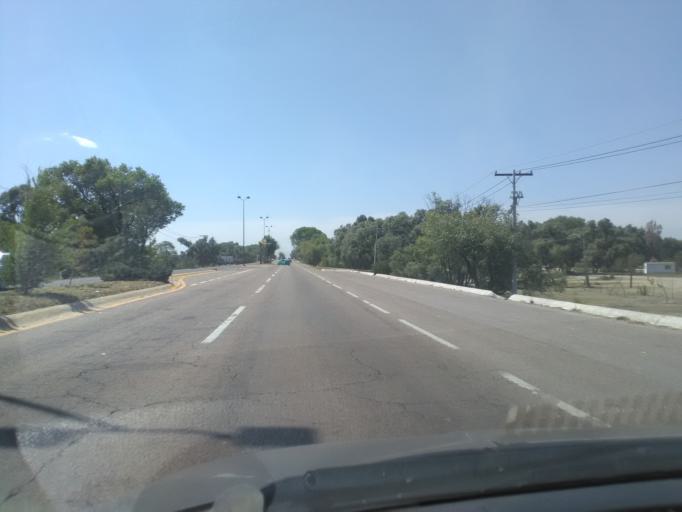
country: MX
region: Durango
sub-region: Durango
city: Jose Refugio Salcido
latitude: 24.0248
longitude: -104.5595
